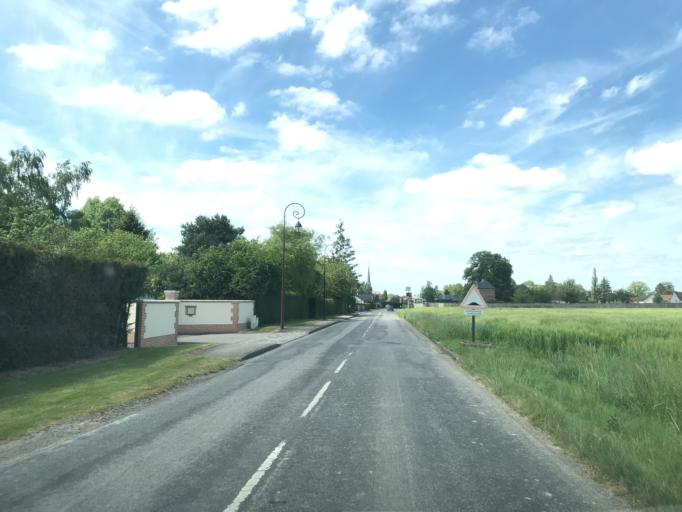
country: FR
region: Haute-Normandie
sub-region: Departement de l'Eure
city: Nassandres
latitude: 49.1637
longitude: 0.7906
